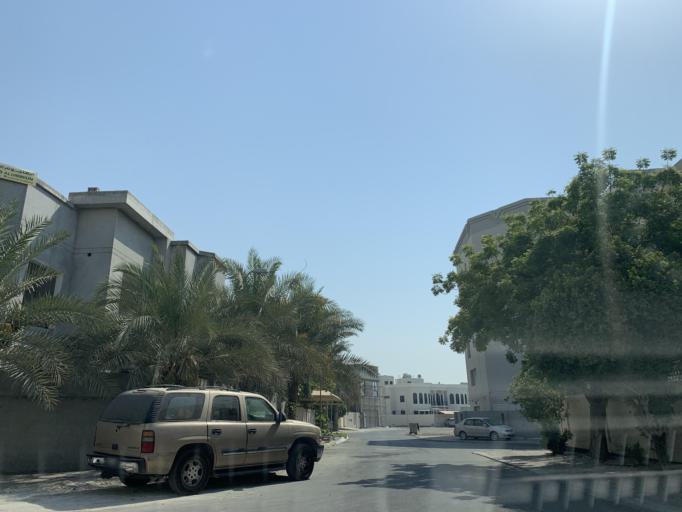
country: BH
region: Northern
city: Madinat `Isa
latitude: 26.1919
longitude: 50.5086
